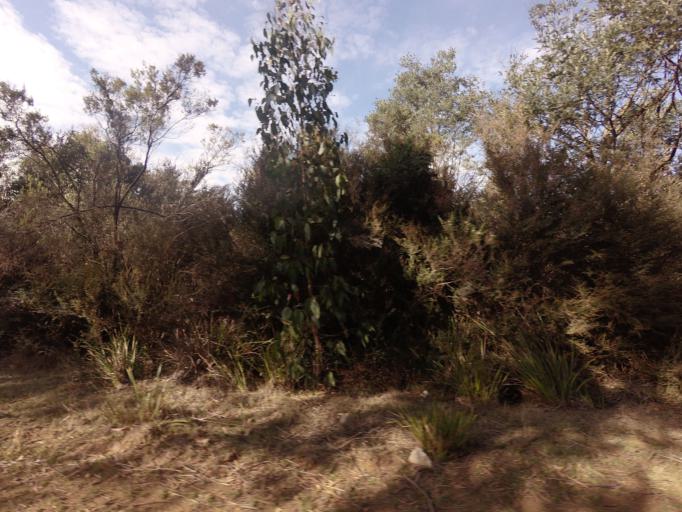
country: AU
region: Tasmania
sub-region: Sorell
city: Sorell
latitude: -42.5009
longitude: 147.4794
